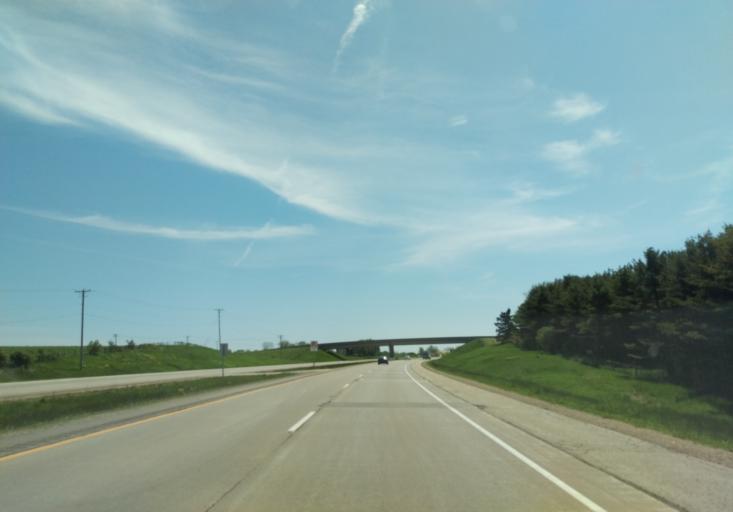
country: US
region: Wisconsin
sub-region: Dane County
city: Mount Horeb
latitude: 43.0039
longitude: -89.6841
